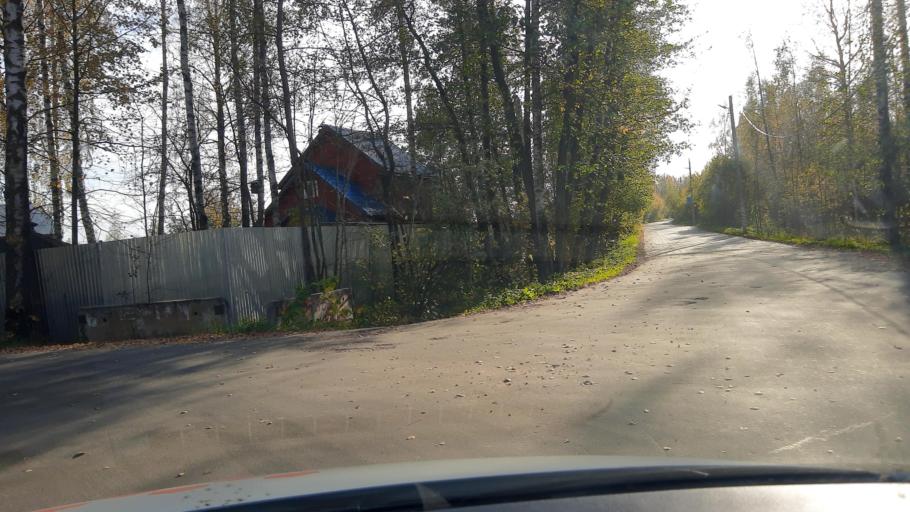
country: RU
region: Moskovskaya
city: Imeni Vorovskogo
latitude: 55.7837
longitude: 38.3606
